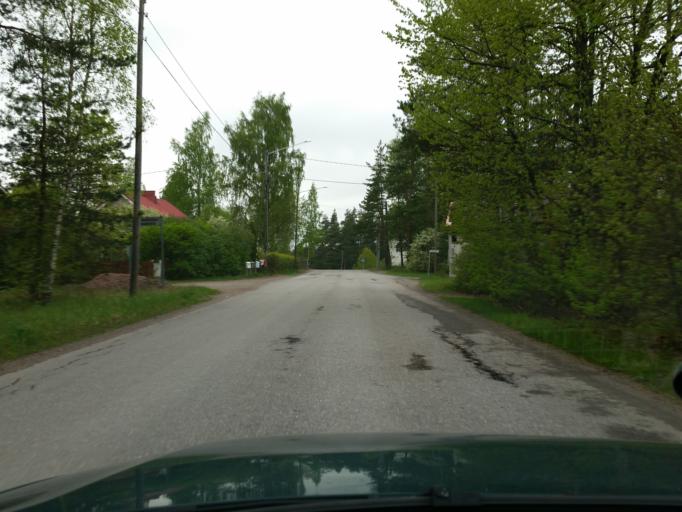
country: FI
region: Uusimaa
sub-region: Raaseporin
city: Inga
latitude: 60.1367
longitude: 23.8659
